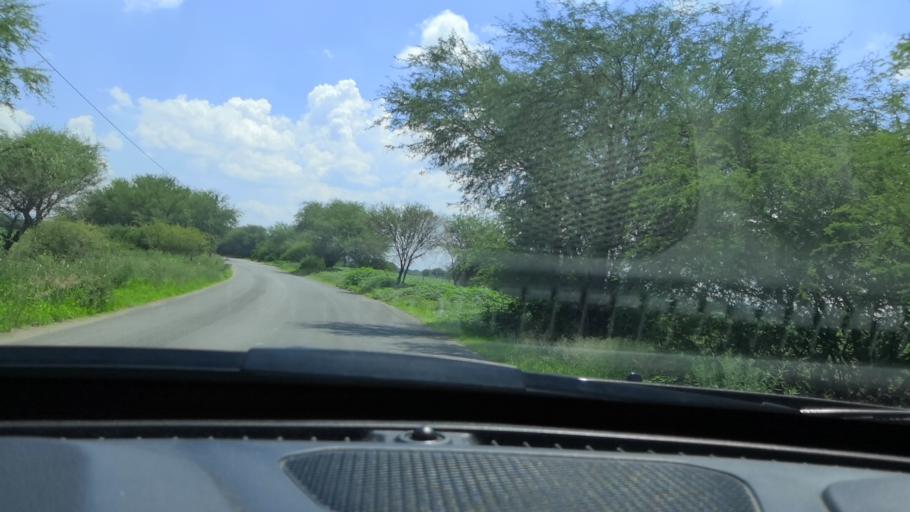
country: MX
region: Guanajuato
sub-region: Leon
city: Plan Guanajuato (La Sandia)
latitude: 20.9441
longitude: -101.6226
